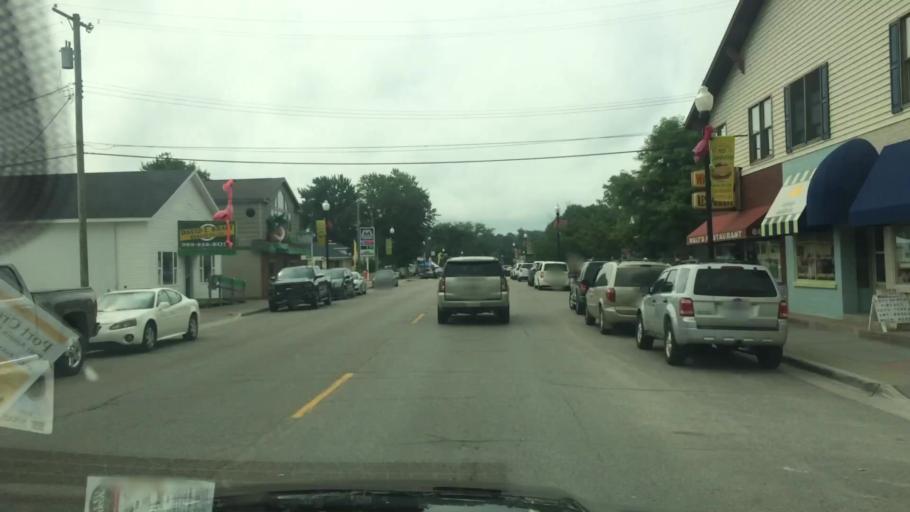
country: US
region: Michigan
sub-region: Huron County
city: Pigeon
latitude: 43.9424
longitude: -83.2727
